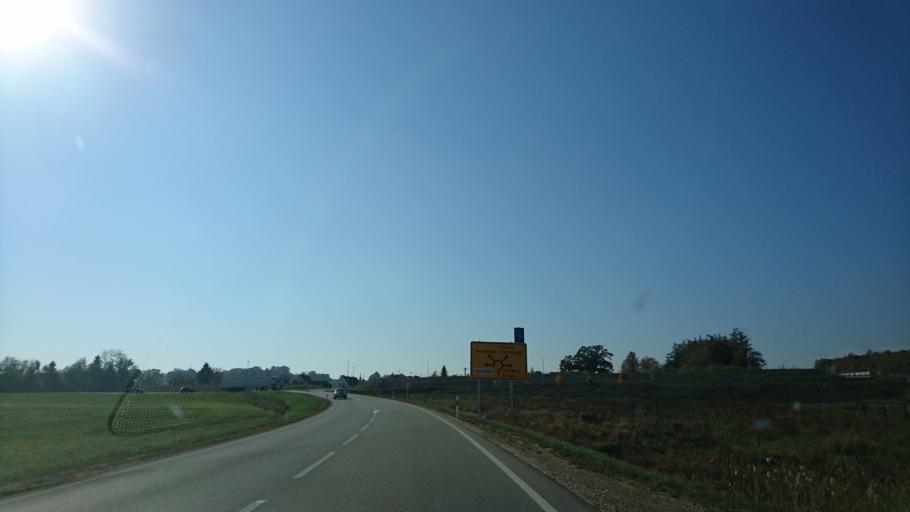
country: DE
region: Bavaria
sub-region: Swabia
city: Zusmarshausen
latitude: 48.4089
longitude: 10.5904
